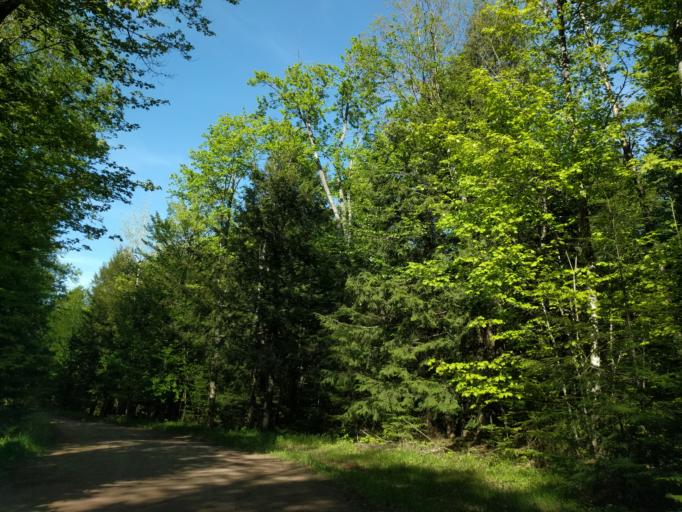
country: US
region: Michigan
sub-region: Marquette County
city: Gwinn
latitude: 46.2578
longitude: -87.3642
